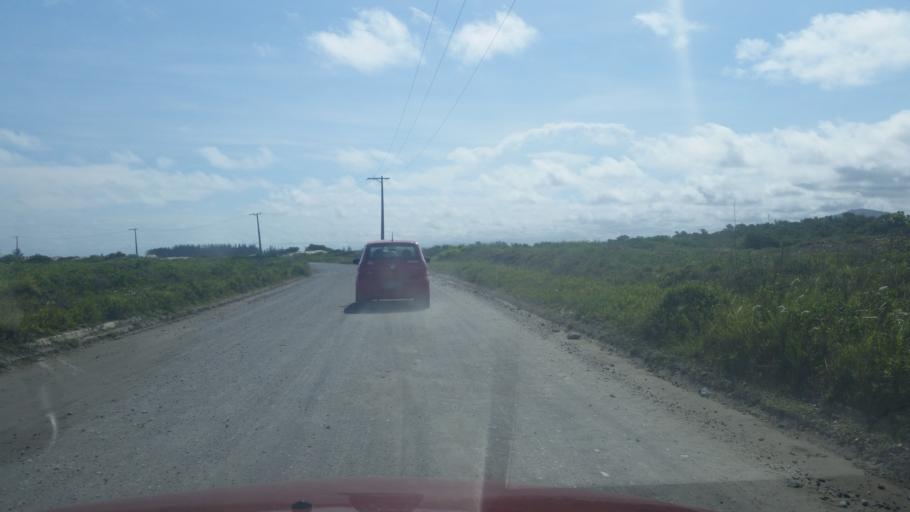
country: BR
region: Sao Paulo
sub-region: Iguape
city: Iguape
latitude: -24.7028
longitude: -47.4687
